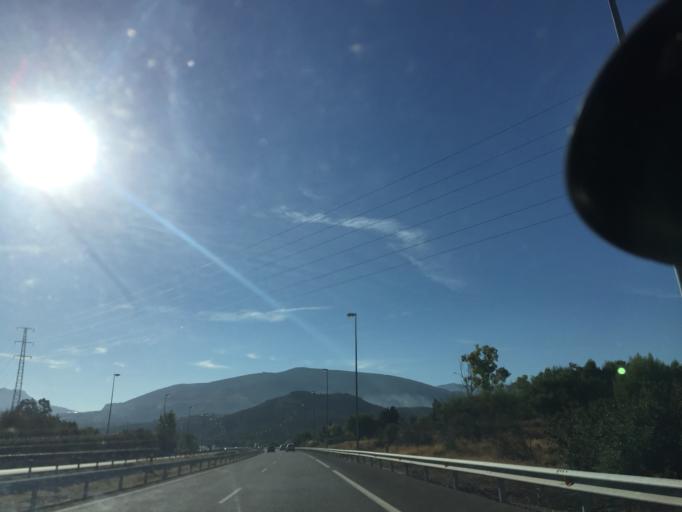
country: ES
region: Andalusia
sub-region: Provincia de Jaen
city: Jaen
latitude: 37.7833
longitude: -3.7545
